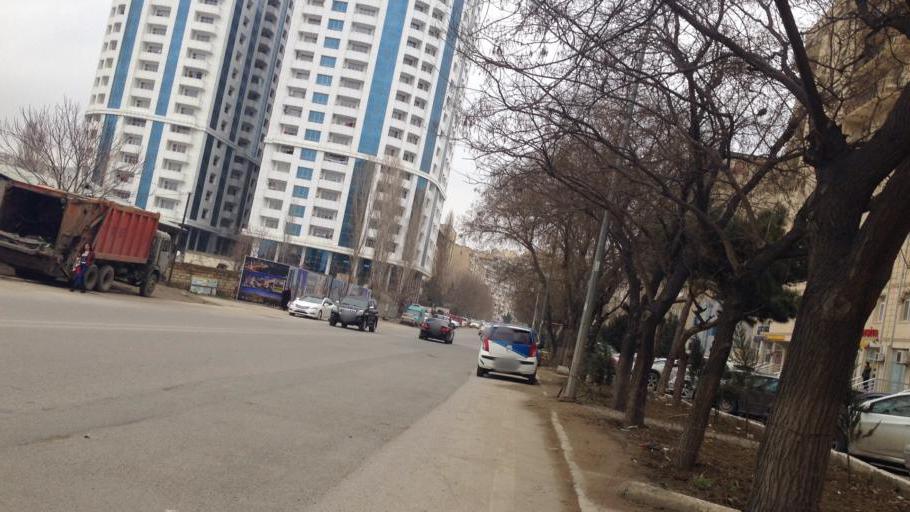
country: AZ
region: Baki
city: Badamdar
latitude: 40.3871
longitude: 49.8159
